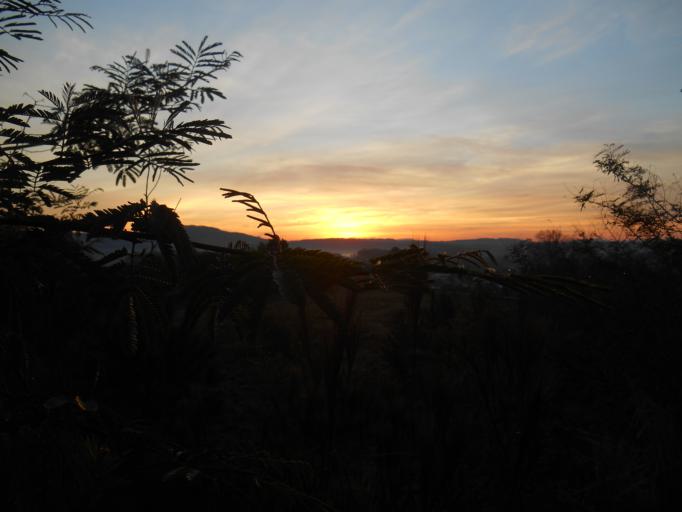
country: BR
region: Rio Grande do Sul
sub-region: Parobe
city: Parobe
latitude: -29.6296
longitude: -50.8217
